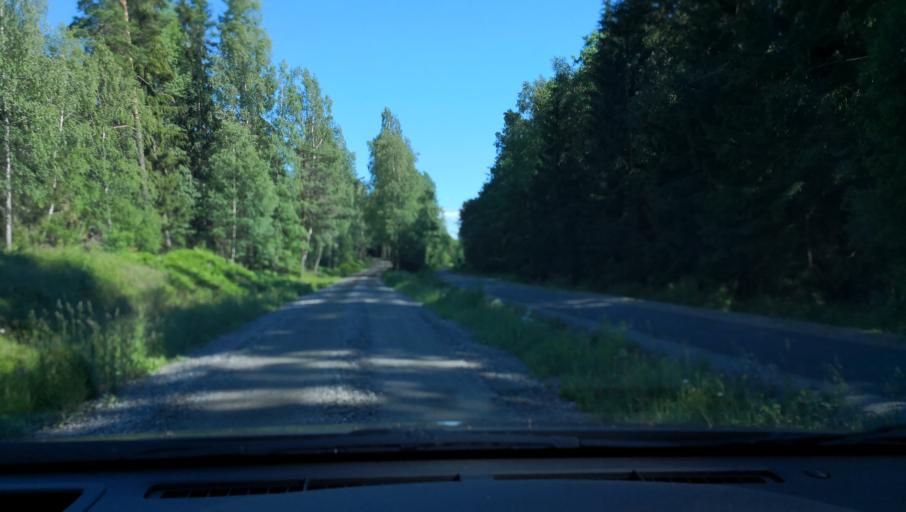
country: SE
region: Soedermanland
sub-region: Eskilstuna Kommun
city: Eskilstuna
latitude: 59.3309
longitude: 16.5802
